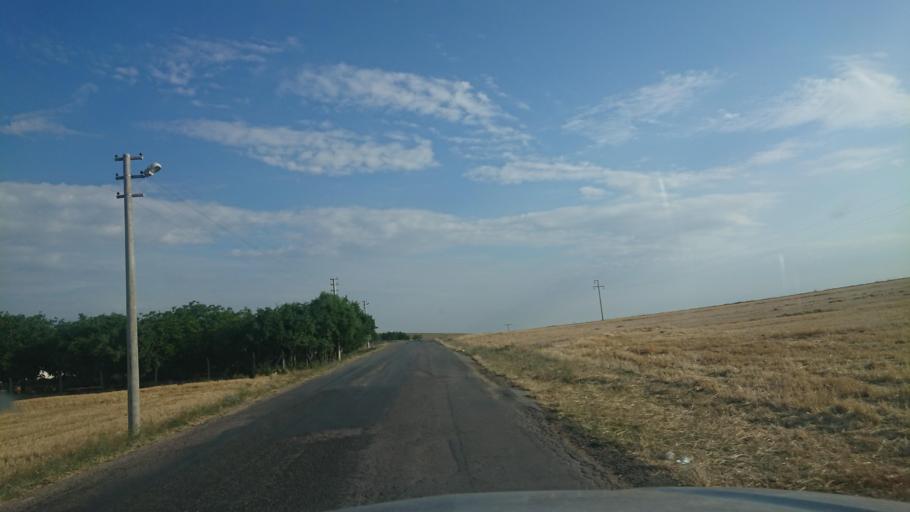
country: TR
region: Aksaray
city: Ortakoy
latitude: 38.7764
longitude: 34.0612
